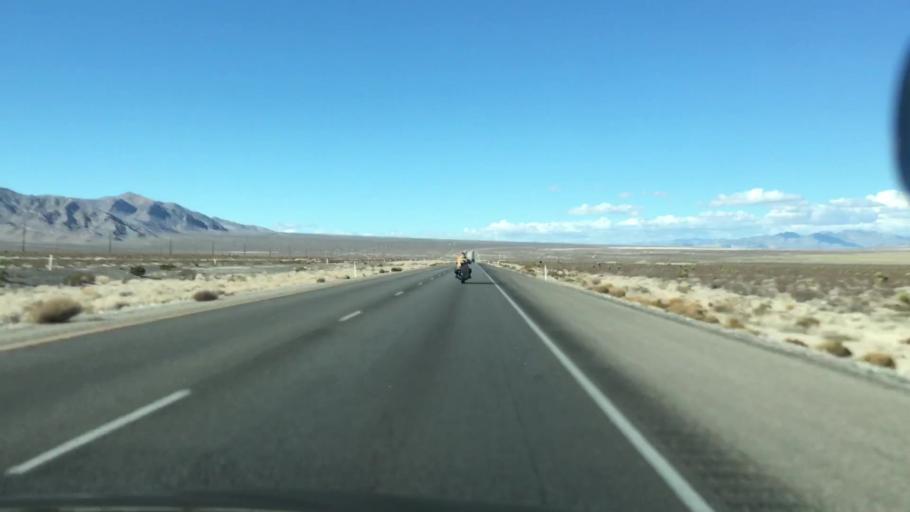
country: US
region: Nevada
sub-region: Clark County
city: Summerlin South
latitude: 36.3879
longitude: -115.3821
